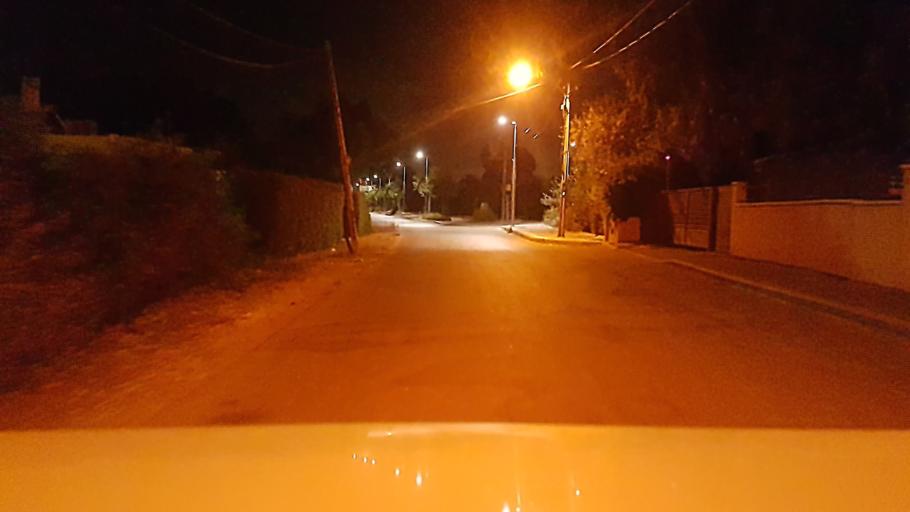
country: IL
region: Central District
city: Nehalim
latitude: 32.0777
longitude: 34.9300
